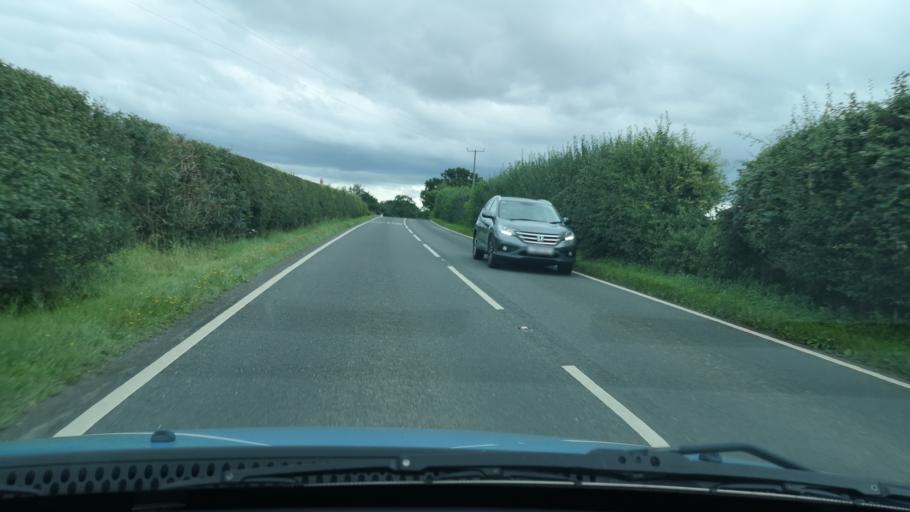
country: GB
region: England
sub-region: City and Borough of Wakefield
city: Featherstone
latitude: 53.6595
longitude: -1.3571
